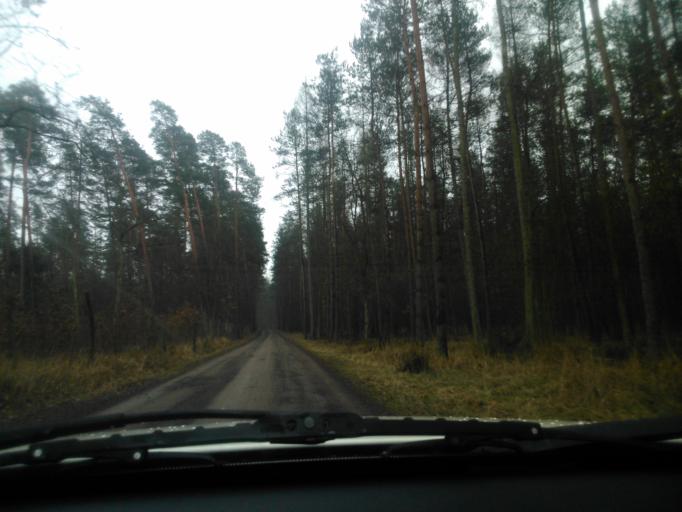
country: PL
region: Kujawsko-Pomorskie
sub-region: Powiat golubsko-dobrzynski
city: Radomin
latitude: 53.1585
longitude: 19.1495
